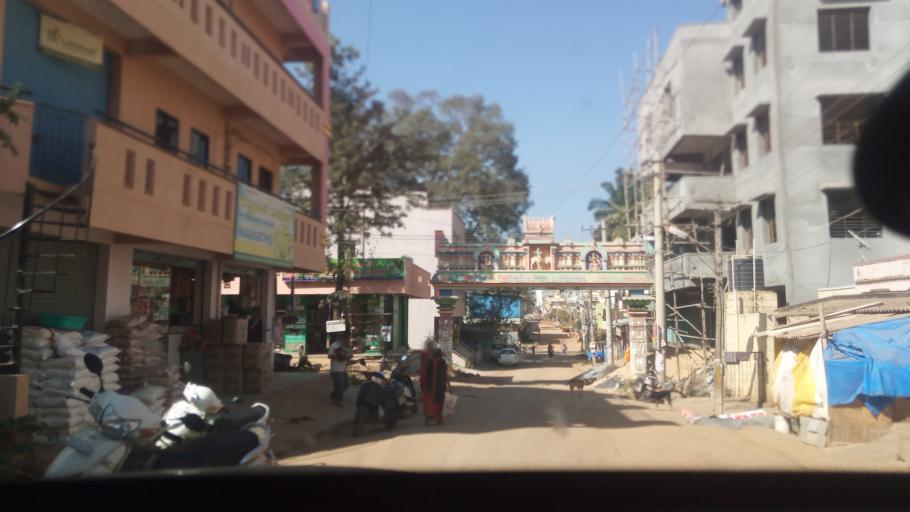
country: IN
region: Karnataka
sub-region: Bangalore Rural
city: Nelamangala
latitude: 13.0374
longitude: 77.4938
